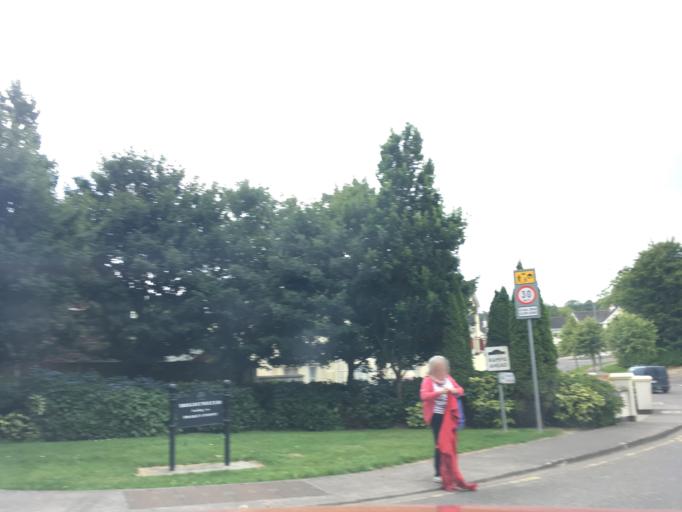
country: IE
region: Munster
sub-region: County Cork
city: Crosshaven
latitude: 51.8002
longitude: -8.2932
